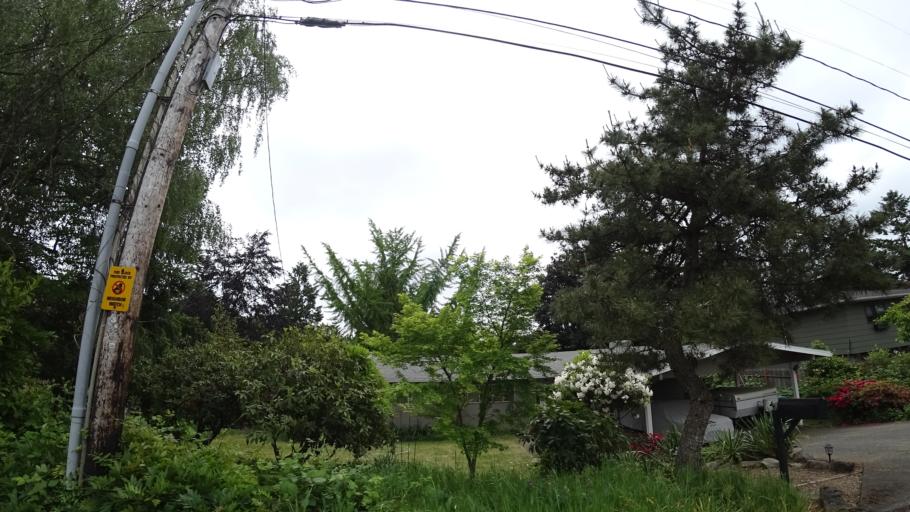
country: US
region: Oregon
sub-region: Multnomah County
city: Portland
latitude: 45.4815
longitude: -122.7013
